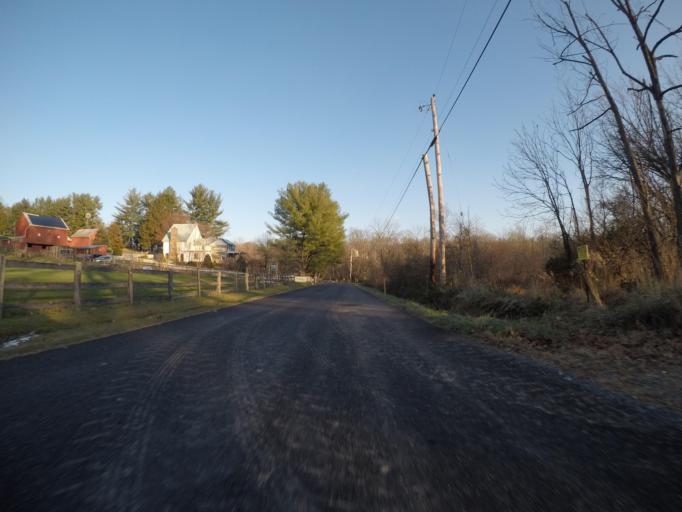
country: US
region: Maryland
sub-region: Carroll County
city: Hampstead
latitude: 39.5867
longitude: -76.8900
